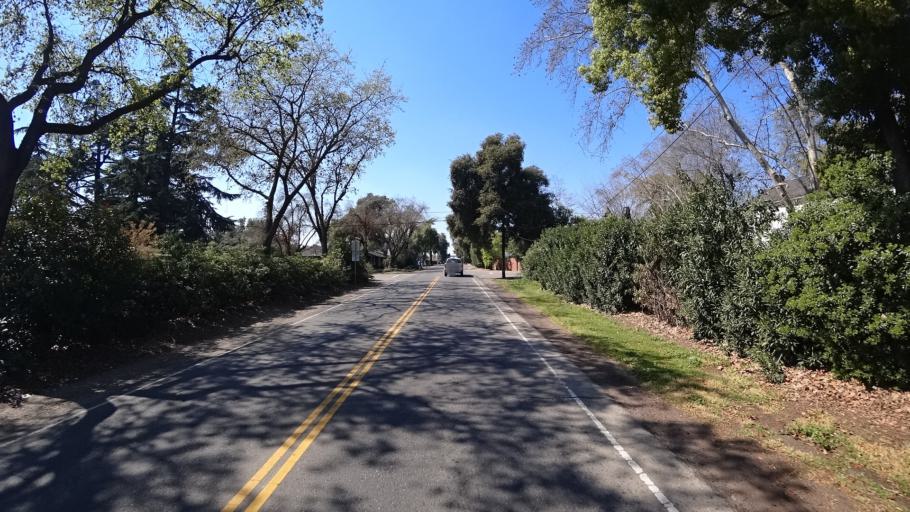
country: US
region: California
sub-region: Fresno County
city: Fresno
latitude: 36.7940
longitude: -119.8060
